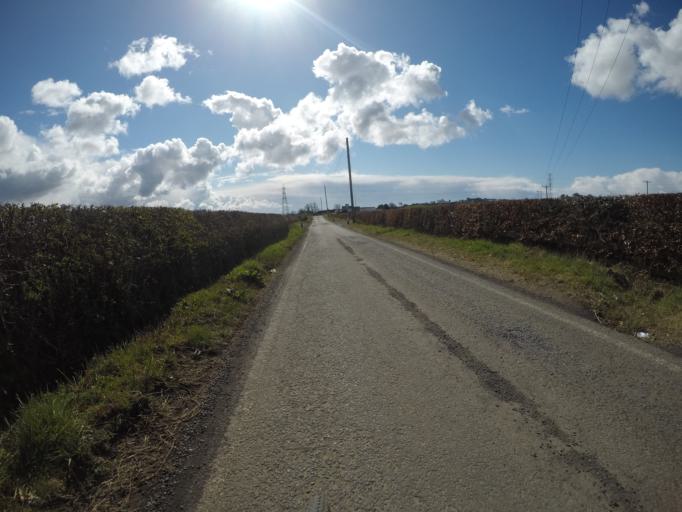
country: GB
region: Scotland
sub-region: North Ayrshire
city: Kilwinning
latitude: 55.6742
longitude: -4.7227
